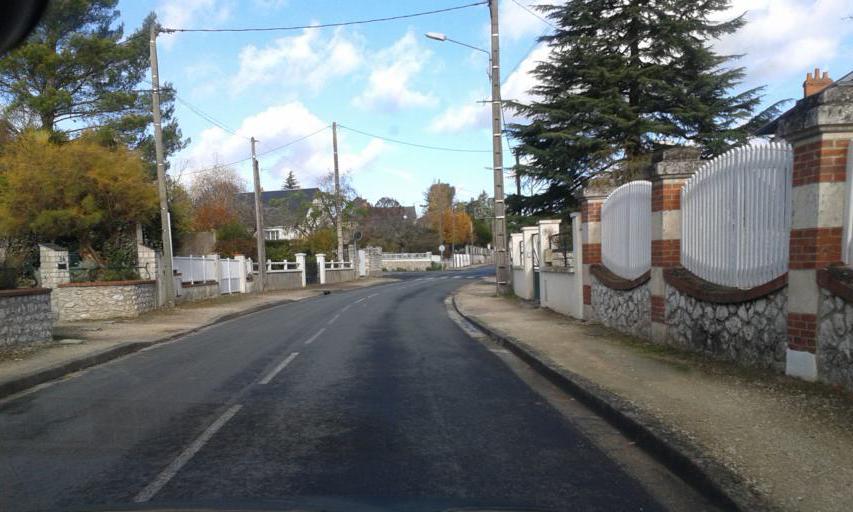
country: FR
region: Centre
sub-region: Departement du Loiret
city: Beaugency
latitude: 47.7711
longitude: 1.6289
